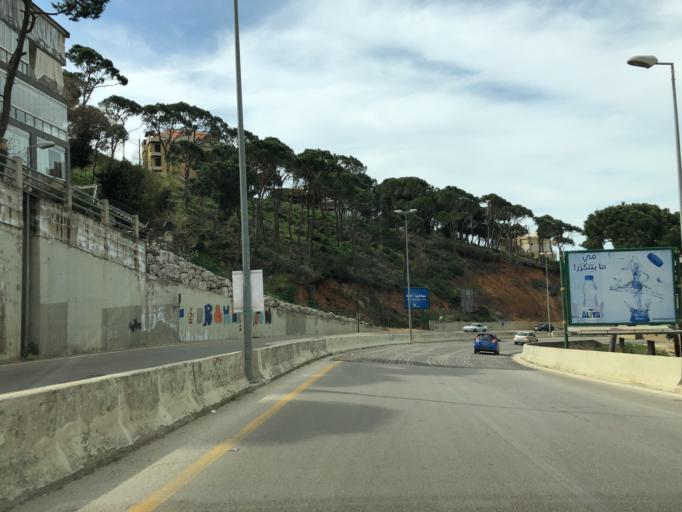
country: LB
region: Mont-Liban
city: Bhamdoun el Mhatta
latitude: 33.8898
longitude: 35.6620
